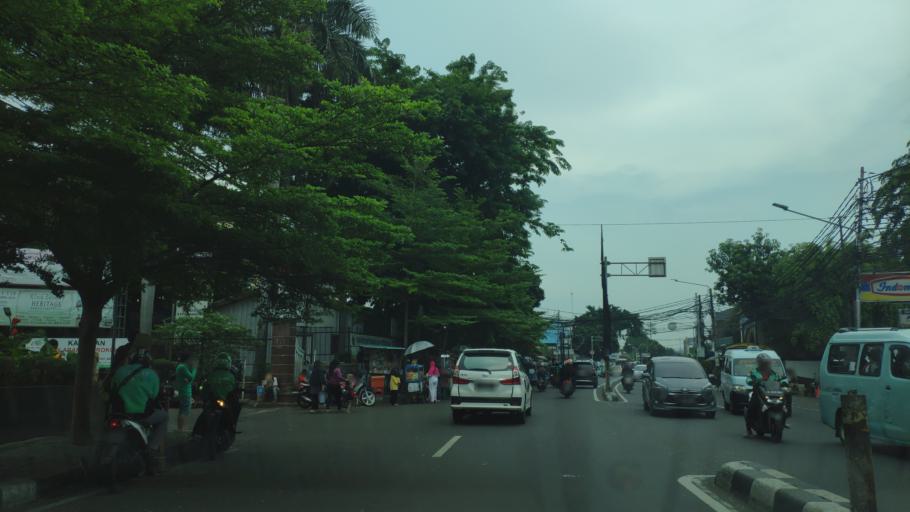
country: ID
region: Jakarta Raya
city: Jakarta
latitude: -6.1931
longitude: 106.8055
